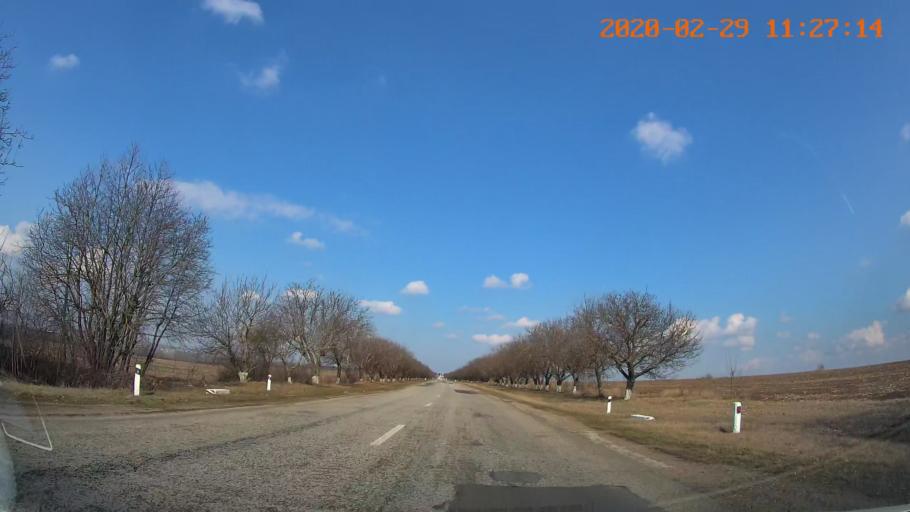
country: MD
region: Telenesti
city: Cocieri
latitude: 47.4651
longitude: 29.1433
